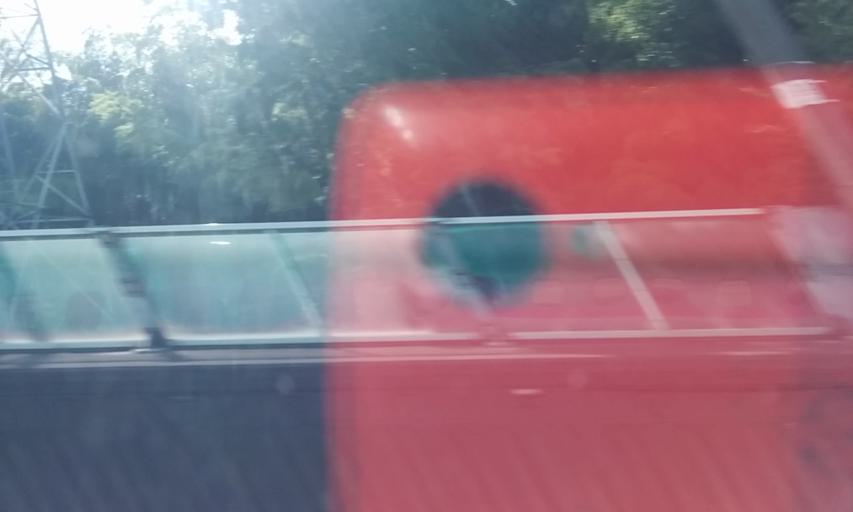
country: JP
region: Tochigi
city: Yaita
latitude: 36.7636
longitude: 139.9449
